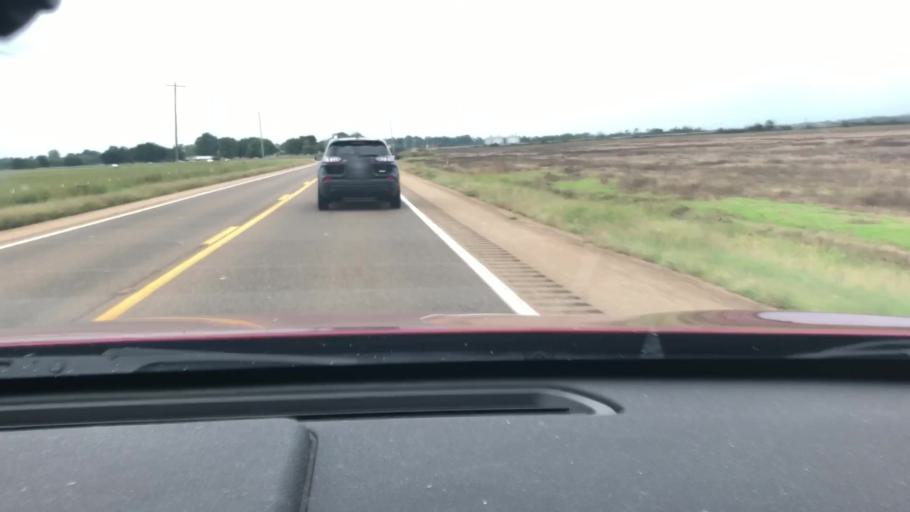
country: US
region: Arkansas
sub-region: Lafayette County
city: Lewisville
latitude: 33.3810
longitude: -93.7365
